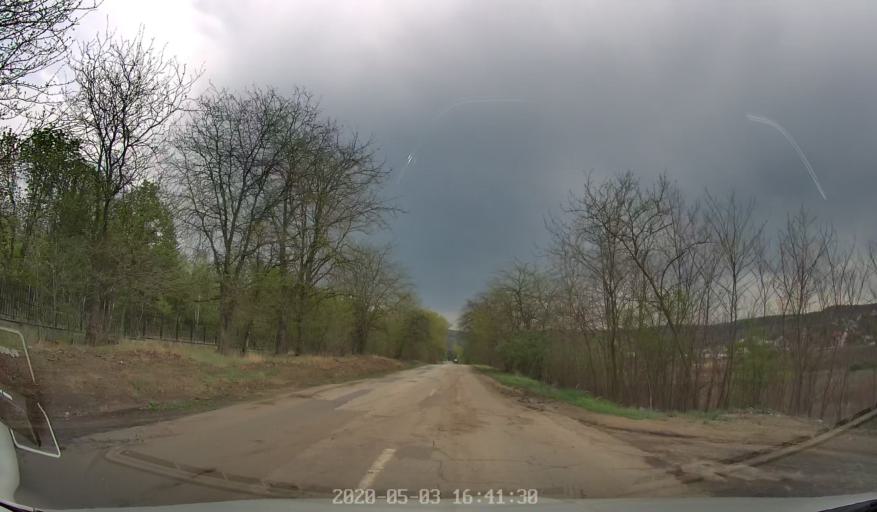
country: MD
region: Stinga Nistrului
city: Bucovat
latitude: 47.1663
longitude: 28.4090
